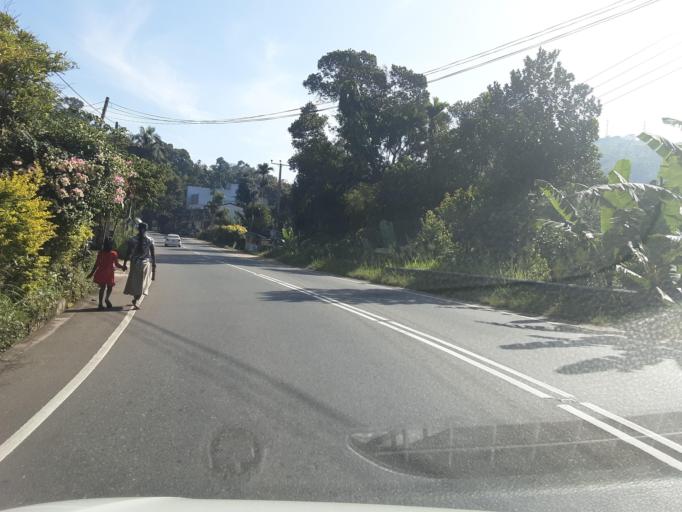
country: LK
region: Uva
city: Badulla
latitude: 6.9738
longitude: 81.0414
